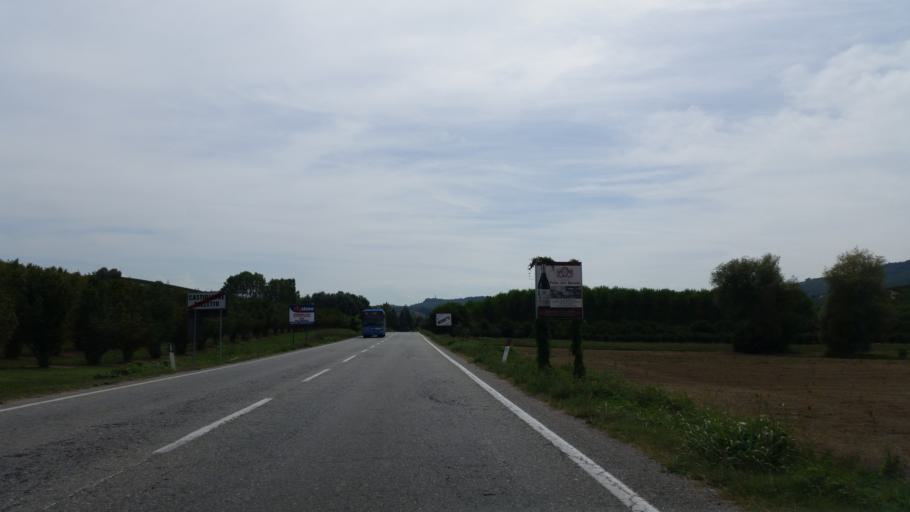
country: IT
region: Piedmont
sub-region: Provincia di Cuneo
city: Castiglione Falletto
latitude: 44.6372
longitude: 7.9698
